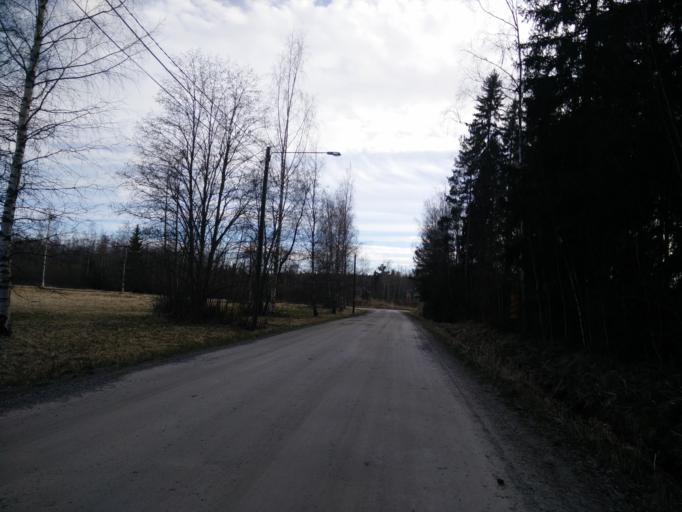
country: FI
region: Pirkanmaa
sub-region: Tampere
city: Orivesi
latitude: 61.6944
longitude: 24.3609
